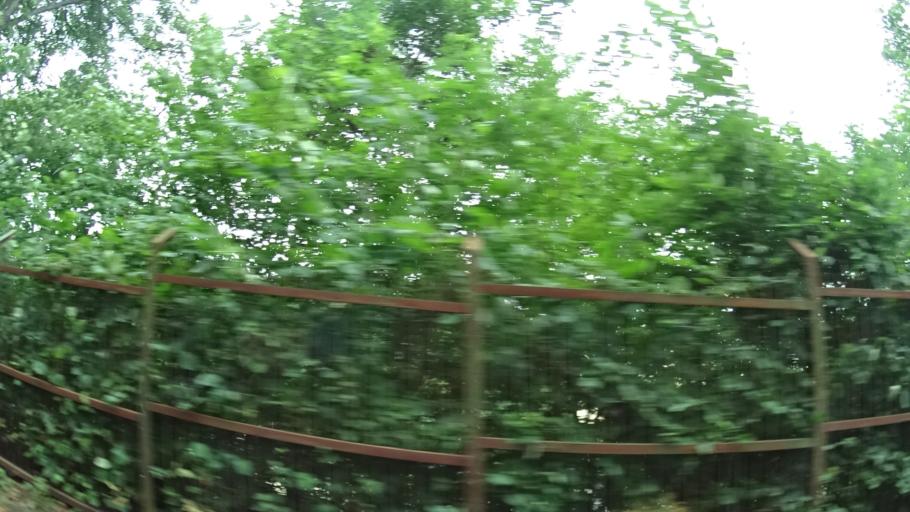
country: DE
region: Saarland
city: Merchweiler
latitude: 49.3440
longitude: 7.0405
